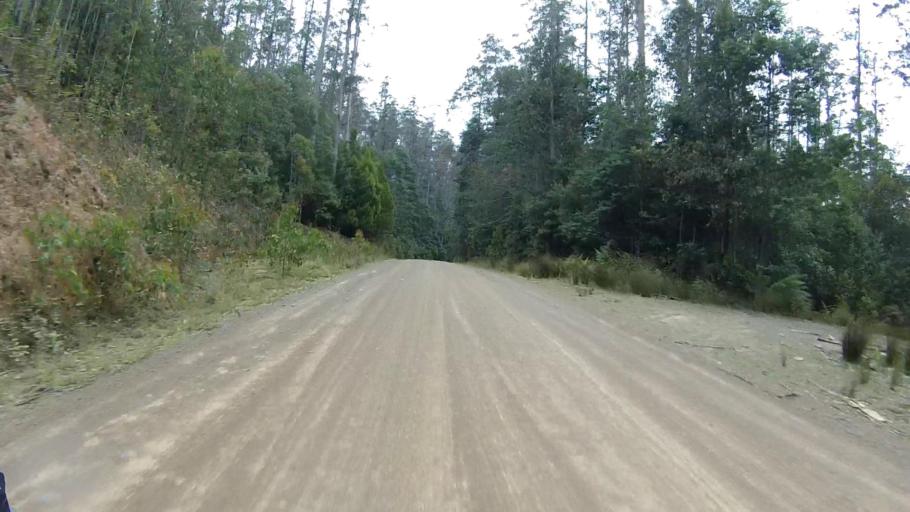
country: AU
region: Tasmania
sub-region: Sorell
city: Sorell
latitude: -42.7136
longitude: 147.8409
